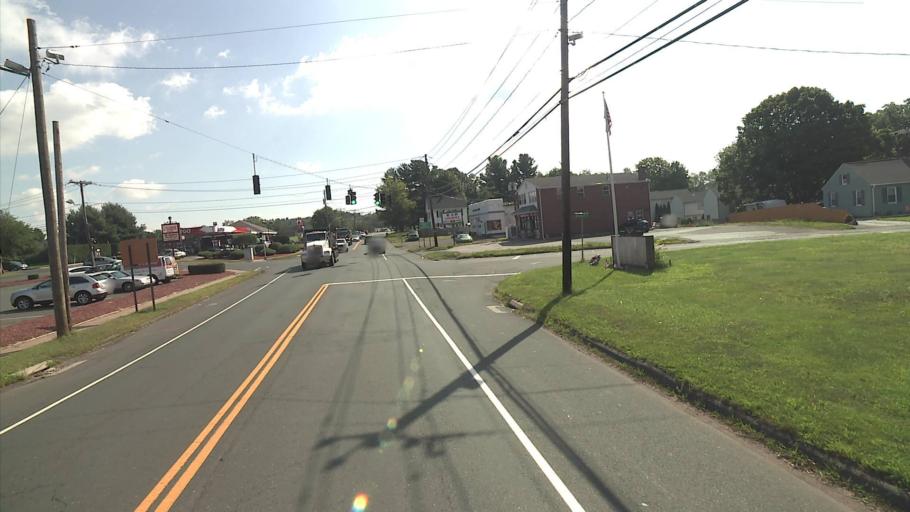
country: US
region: Connecticut
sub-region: Hartford County
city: Hazardville
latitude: 41.9849
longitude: -72.5146
